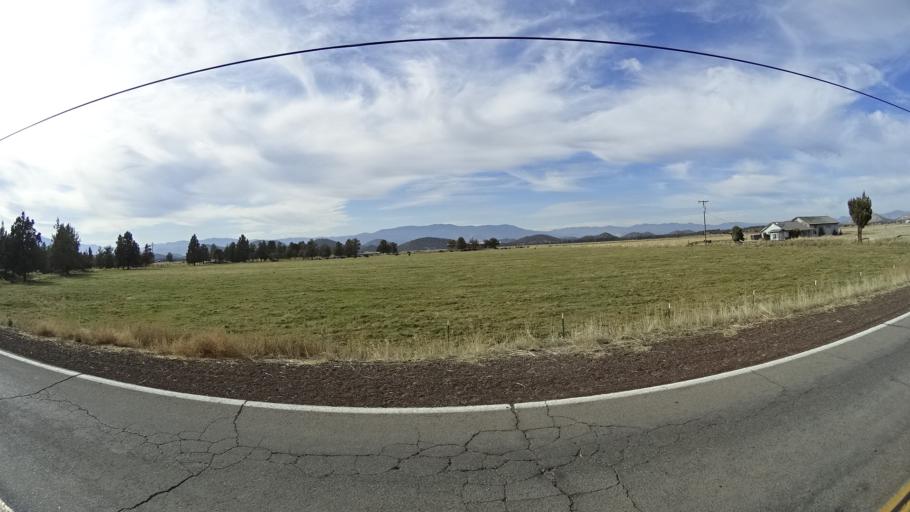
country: US
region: California
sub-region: Siskiyou County
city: Montague
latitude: 41.6106
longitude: -122.4000
